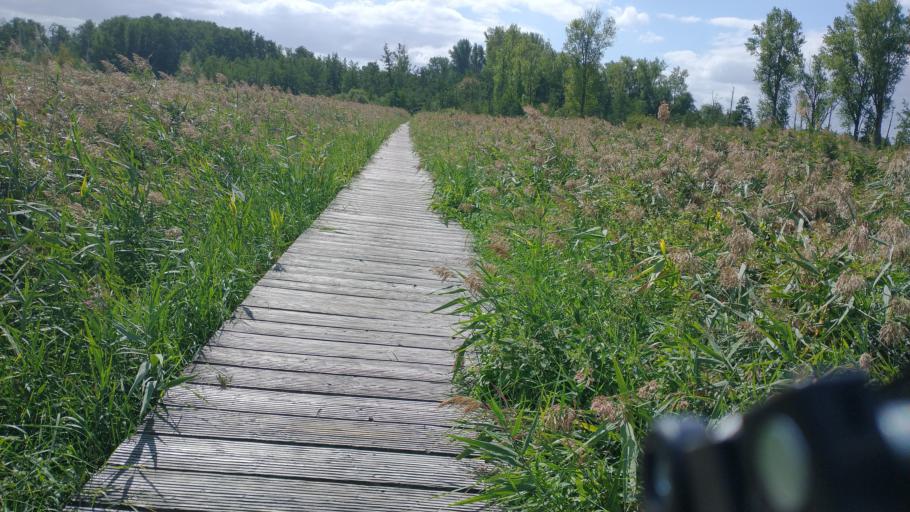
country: DE
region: Schleswig-Holstein
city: Bad Oldesloe
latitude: 53.8189
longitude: 10.3530
